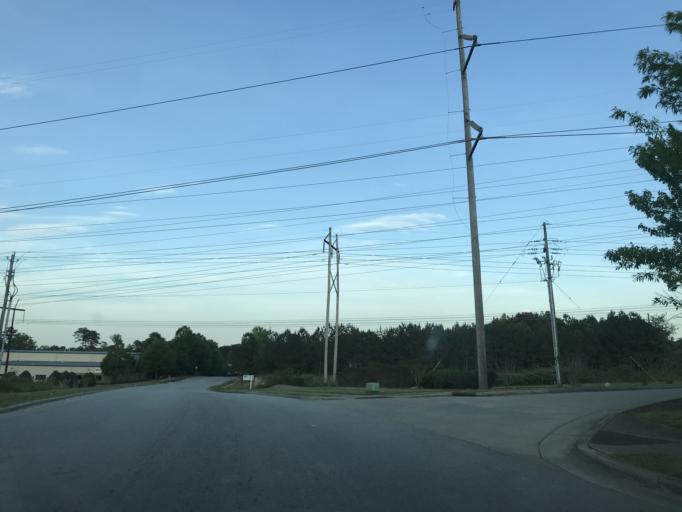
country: US
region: North Carolina
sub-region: Wake County
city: Knightdale
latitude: 35.7672
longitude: -78.5573
